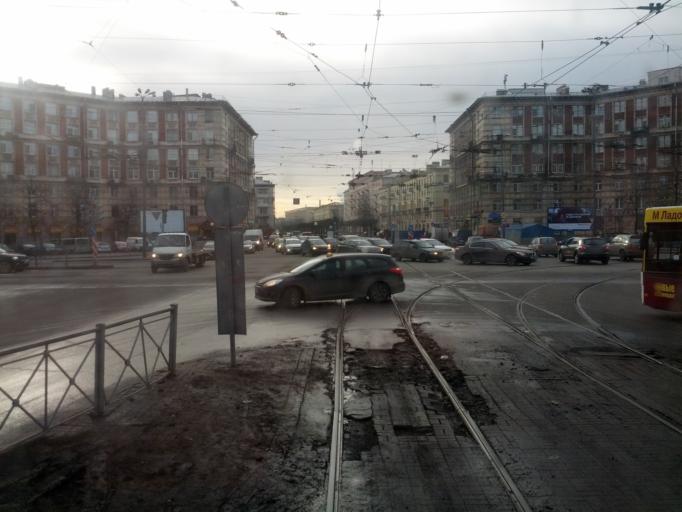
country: RU
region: St.-Petersburg
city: Centralniy
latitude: 59.9293
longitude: 30.4117
